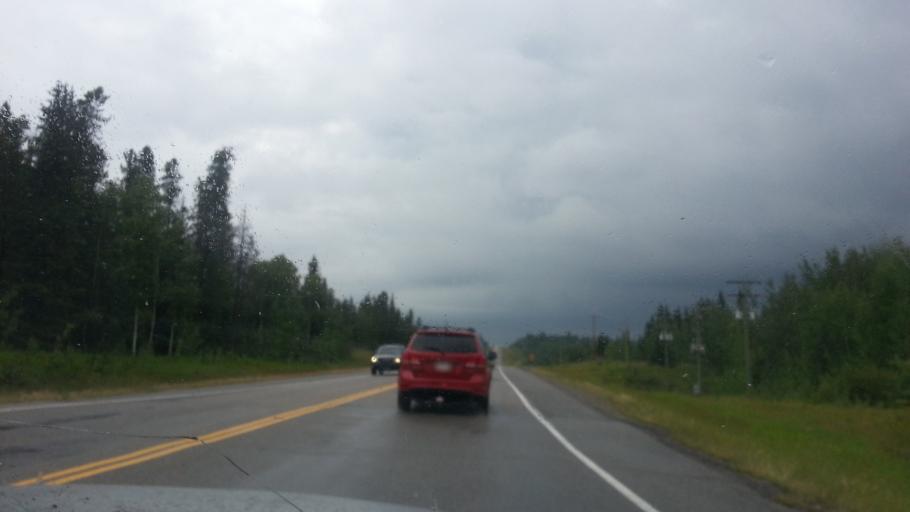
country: CA
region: Alberta
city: Cochrane
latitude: 50.9215
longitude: -114.5600
